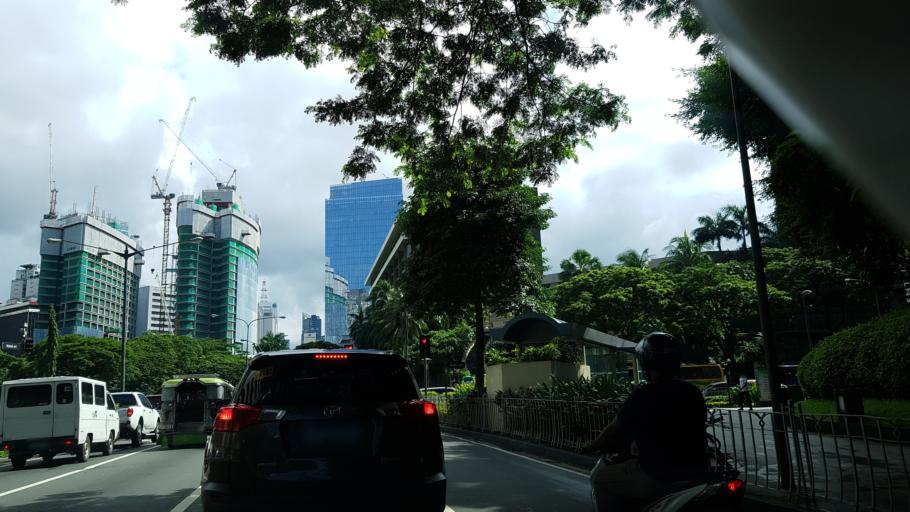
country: PH
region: Metro Manila
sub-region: Makati City
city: Makati City
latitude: 14.5539
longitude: 121.0243
